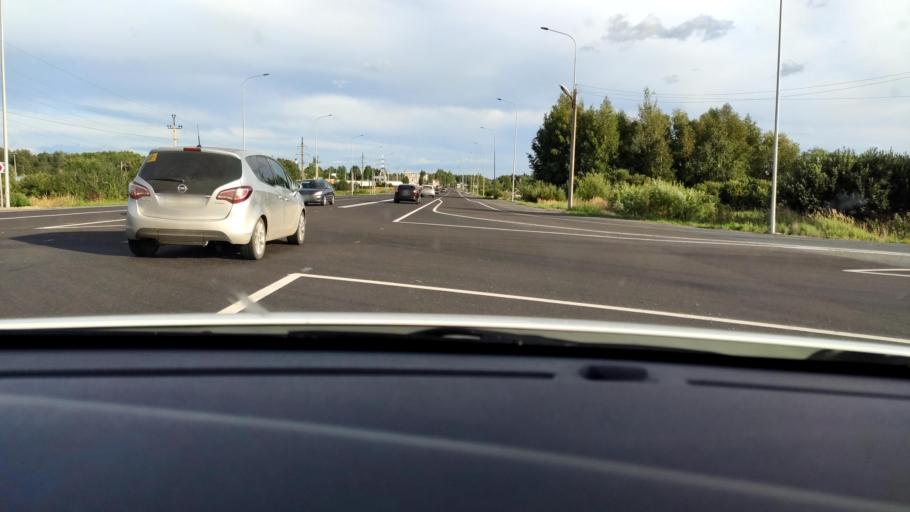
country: RU
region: Mariy-El
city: Krasnogorskiy
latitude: 56.1684
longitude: 48.2830
